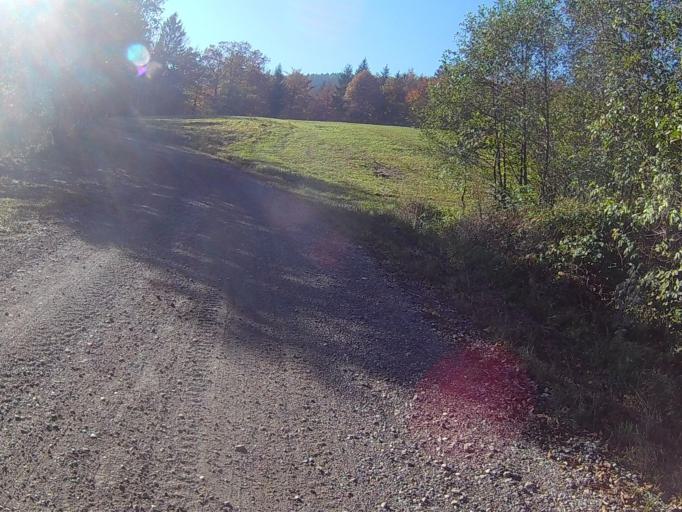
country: SI
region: Maribor
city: Pekre
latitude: 46.5063
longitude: 15.5802
